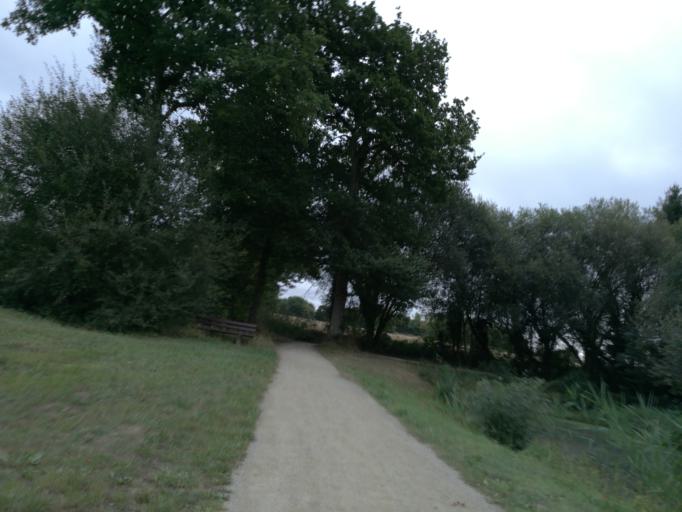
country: FR
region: Brittany
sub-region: Departement d'Ille-et-Vilaine
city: Bedee
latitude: 48.1704
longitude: -1.9527
